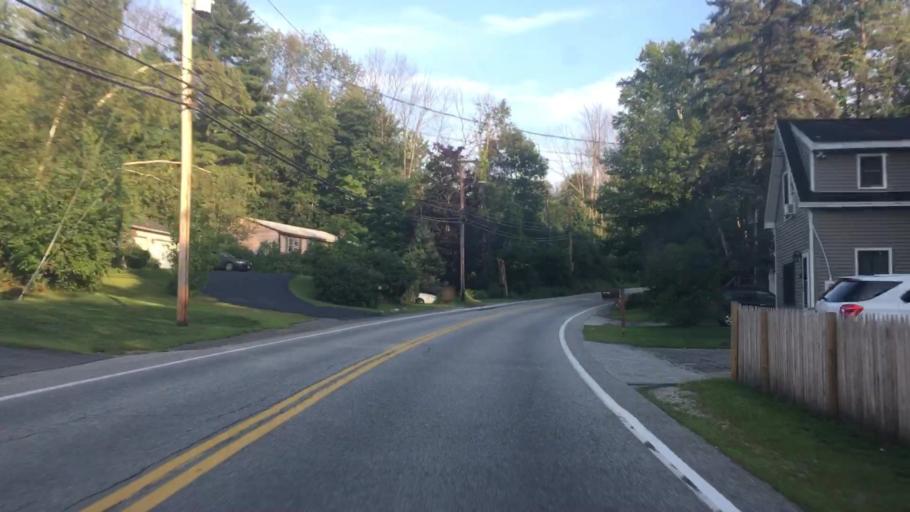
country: US
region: New Hampshire
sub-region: Belknap County
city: Laconia
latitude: 43.5169
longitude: -71.4602
